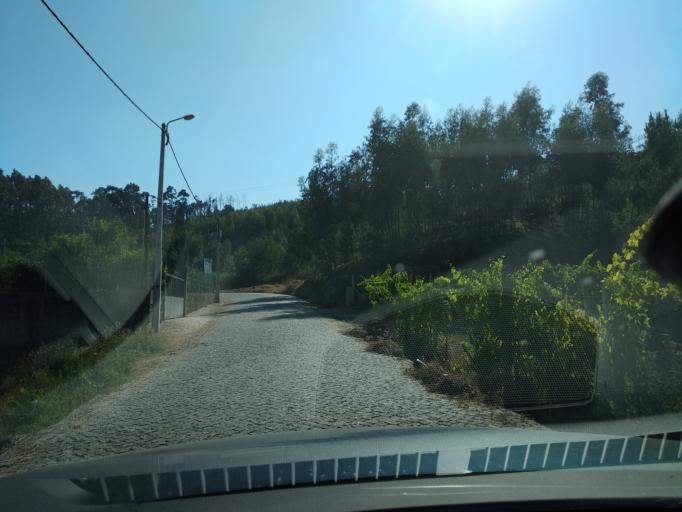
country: PT
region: Porto
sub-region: Paredes
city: Baltar
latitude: 41.2105
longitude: -8.3689
